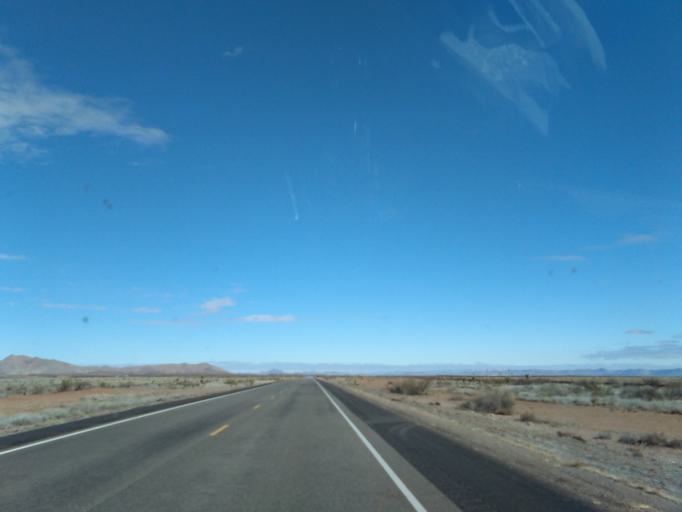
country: US
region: New Mexico
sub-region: Luna County
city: Deming
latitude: 32.3227
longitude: -107.6734
